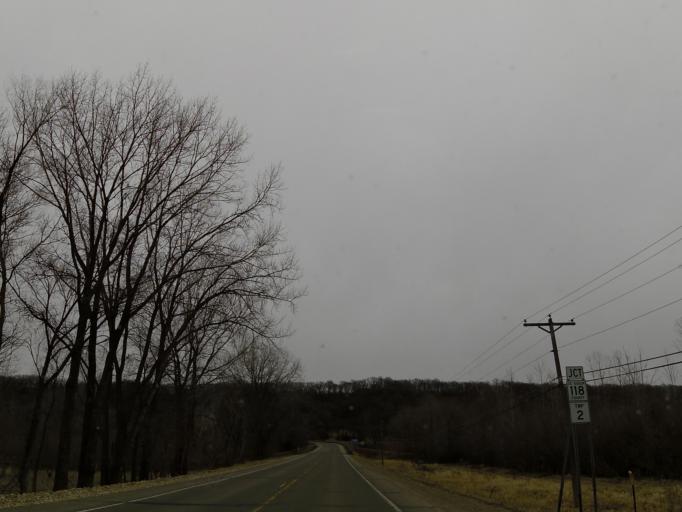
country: US
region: Minnesota
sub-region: Le Sueur County
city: Le Sueur
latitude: 44.5315
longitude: -93.8909
